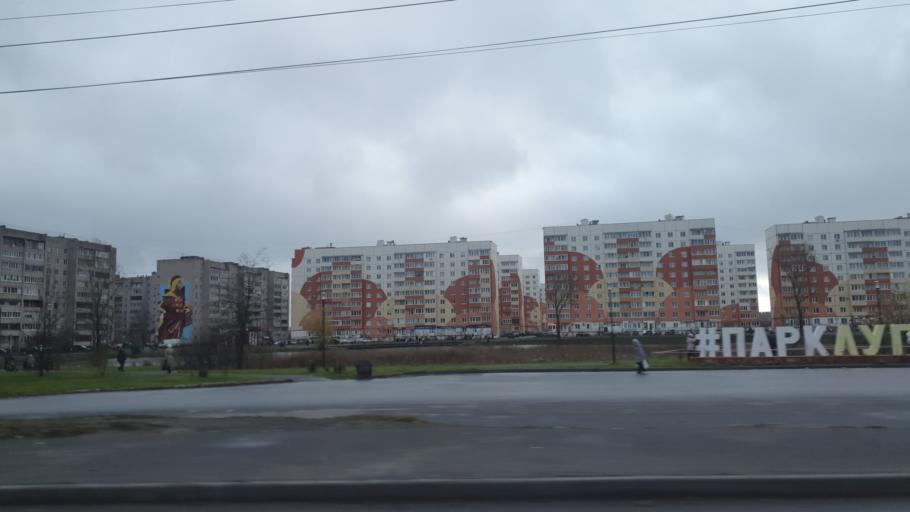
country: RU
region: Novgorod
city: Velikiy Novgorod
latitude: 58.5602
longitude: 31.2750
